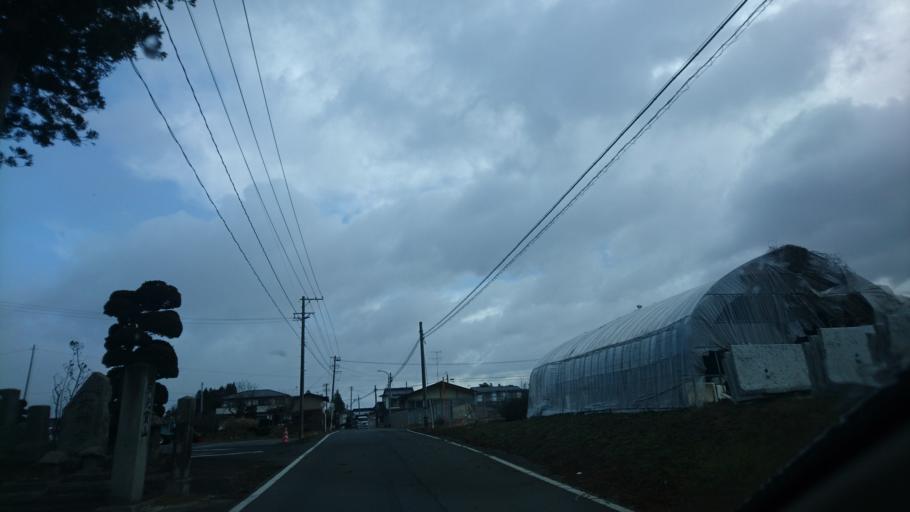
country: JP
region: Iwate
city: Ichinoseki
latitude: 38.7651
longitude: 141.0344
